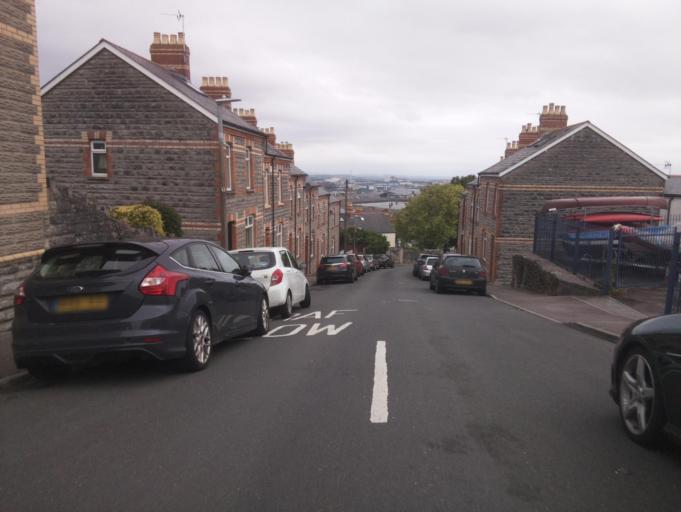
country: GB
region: Wales
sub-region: Vale of Glamorgan
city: Penarth
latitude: 51.4423
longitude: -3.1713
